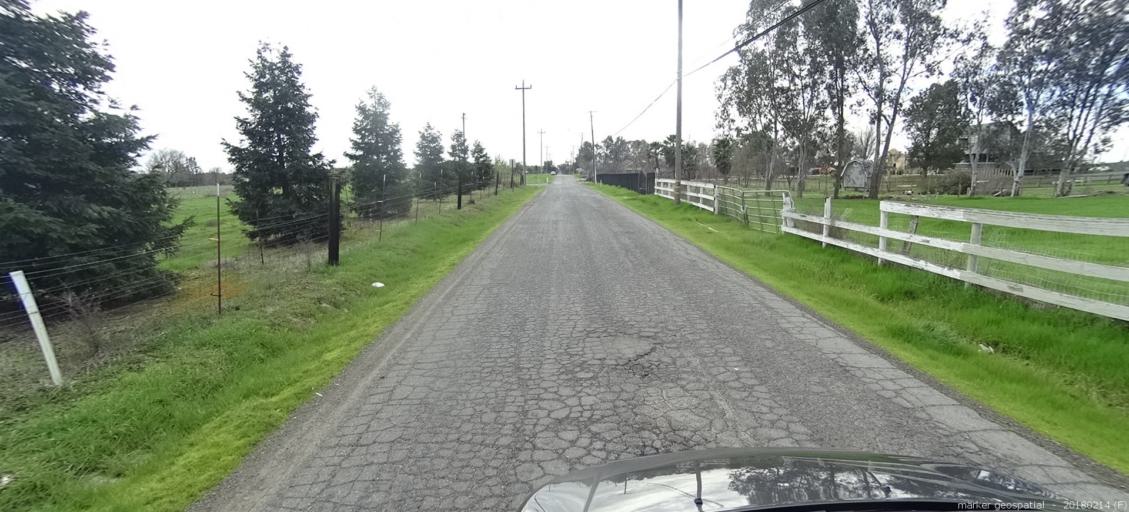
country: US
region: California
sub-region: Sacramento County
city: Rio Linda
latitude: 38.6778
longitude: -121.4754
